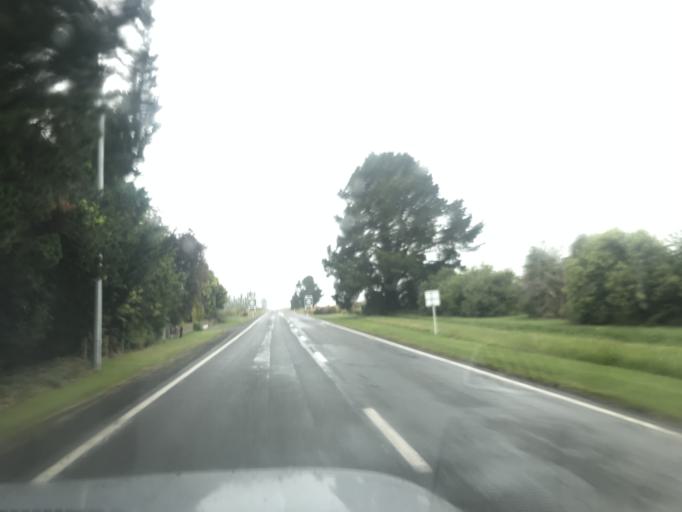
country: NZ
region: Canterbury
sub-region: Selwyn District
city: Darfield
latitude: -43.5019
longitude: 172.2185
